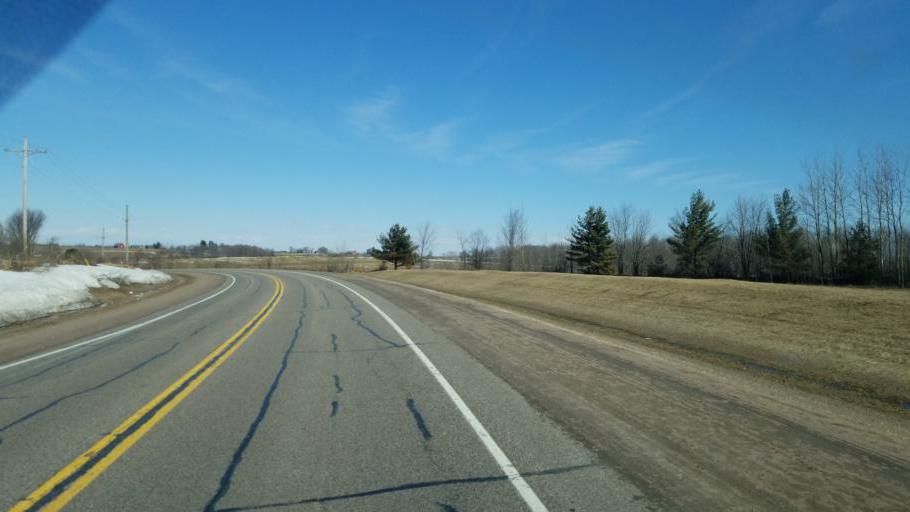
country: US
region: Wisconsin
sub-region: Marathon County
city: Spencer
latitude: 44.5845
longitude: -90.3774
